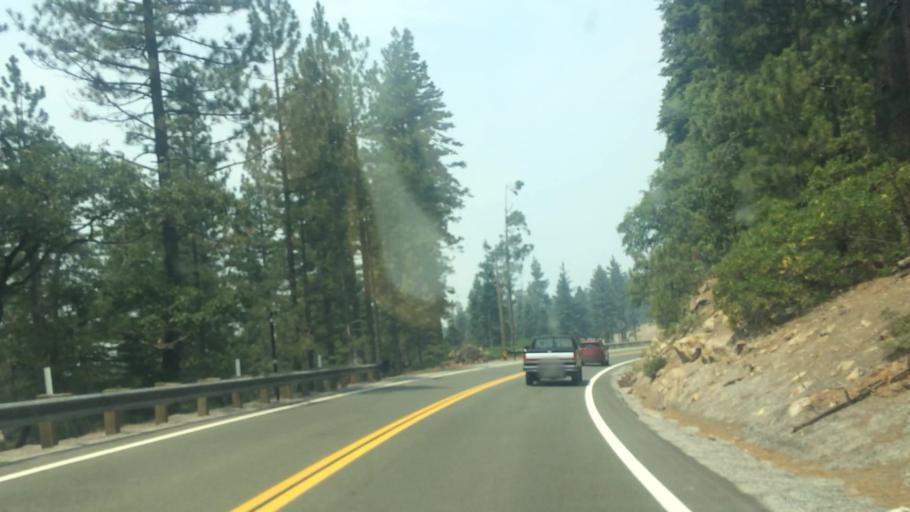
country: US
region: California
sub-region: Amador County
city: Pioneer
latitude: 38.5440
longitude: -120.3502
